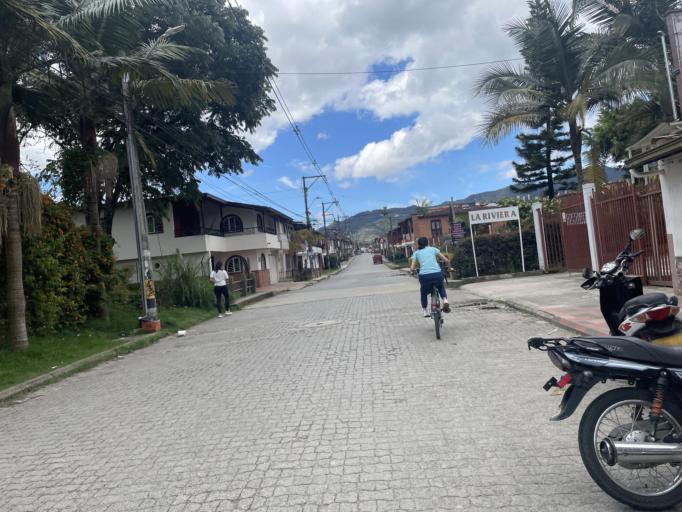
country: CO
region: Antioquia
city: La Ceja
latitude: 6.0265
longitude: -75.4316
